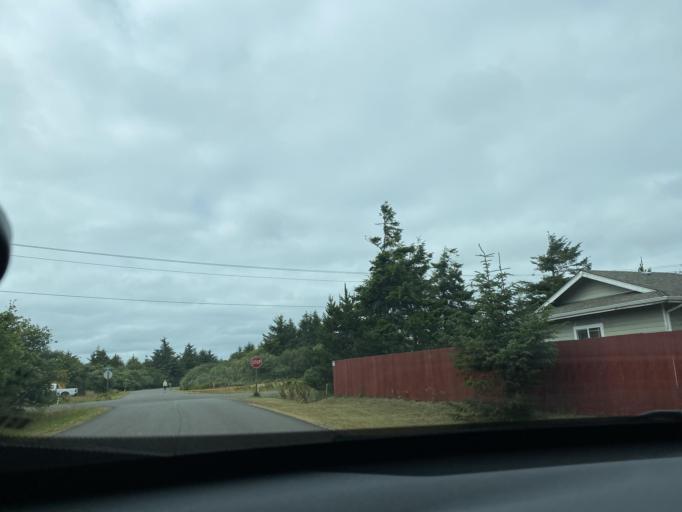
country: US
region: Washington
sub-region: Grays Harbor County
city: Ocean Shores
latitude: 46.9522
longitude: -124.1451
